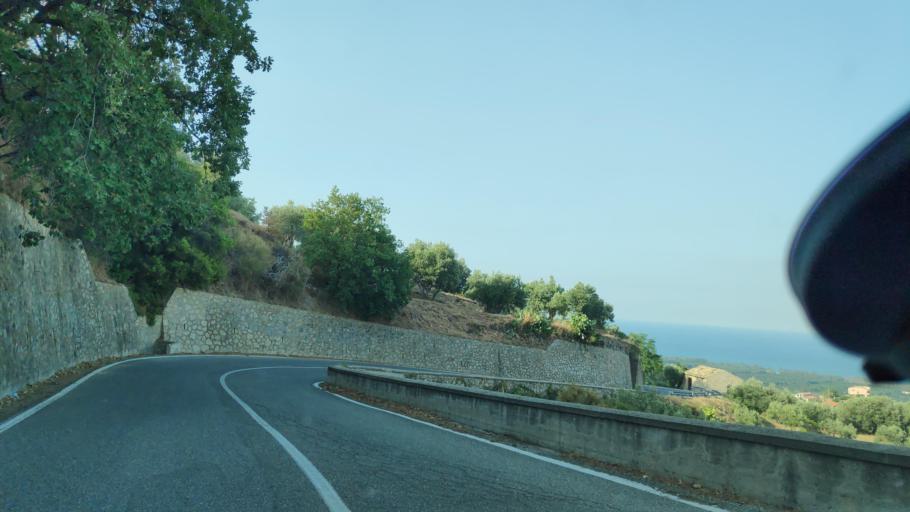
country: IT
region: Calabria
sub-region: Provincia di Catanzaro
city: Sant'Andrea Apostolo dello Ionio
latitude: 38.6189
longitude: 16.5368
